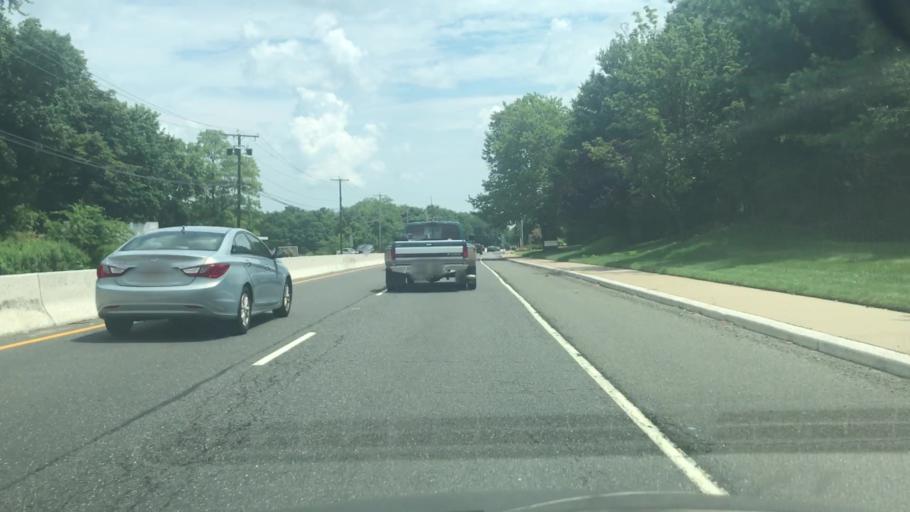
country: US
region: New Jersey
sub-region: Monmouth County
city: Keansburg
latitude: 40.4147
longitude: -74.1553
